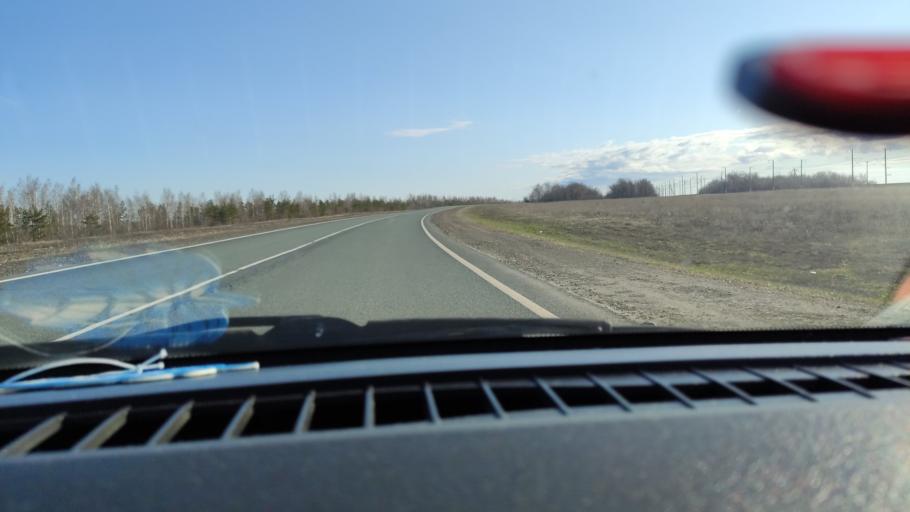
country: RU
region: Samara
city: Syzran'
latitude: 52.8625
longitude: 48.2666
